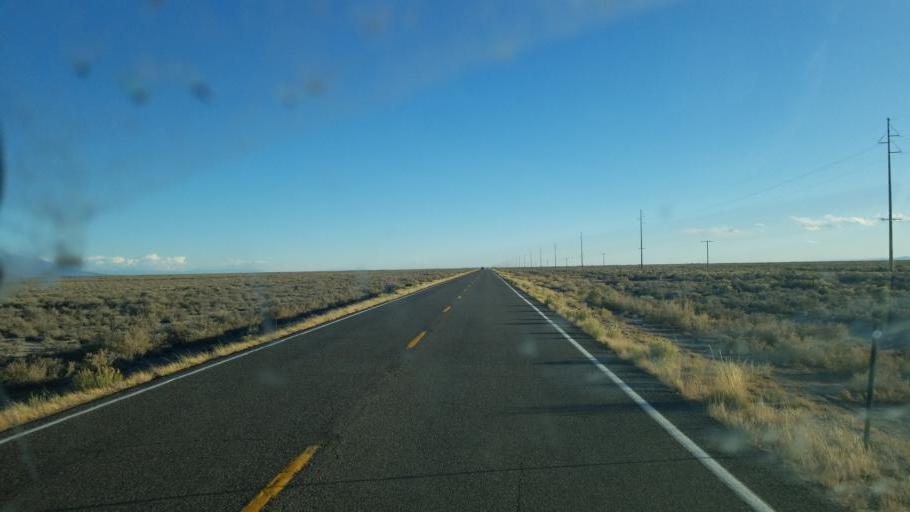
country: US
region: Colorado
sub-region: Saguache County
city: Saguache
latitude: 37.9436
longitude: -105.9024
